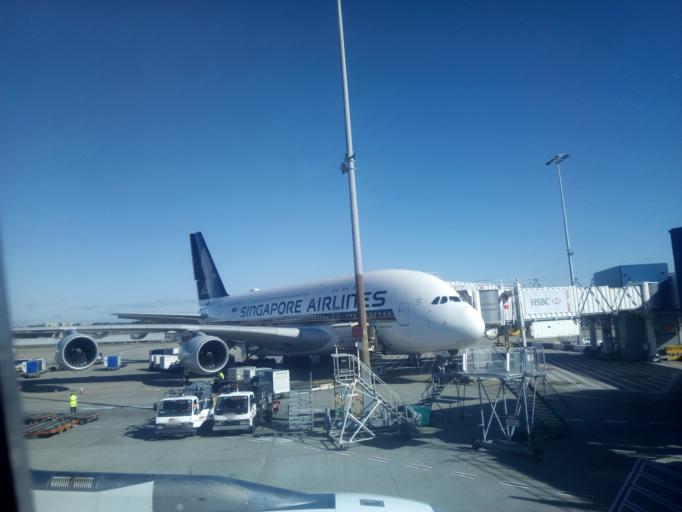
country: AU
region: New South Wales
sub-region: Rockdale
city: Arncliffe
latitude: -33.9404
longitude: 151.1645
